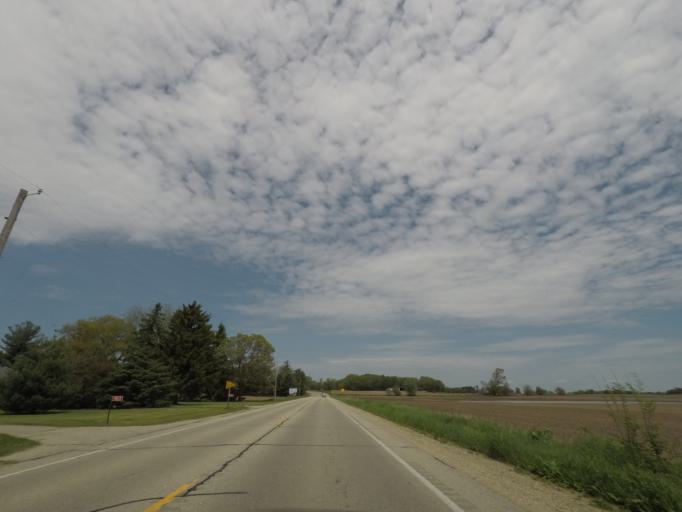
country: US
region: Wisconsin
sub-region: Rock County
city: Evansville
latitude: 42.8143
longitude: -89.2991
